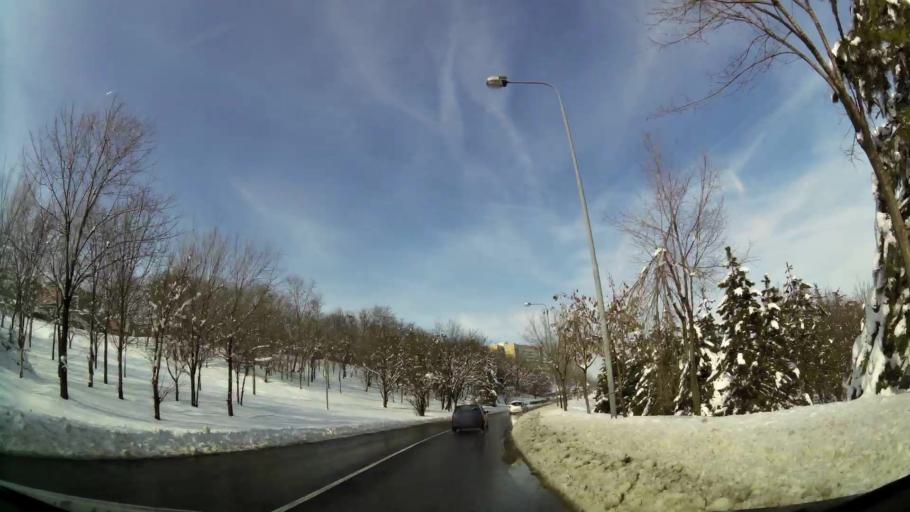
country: RS
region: Central Serbia
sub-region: Belgrade
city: Zvezdara
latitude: 44.7867
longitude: 20.5280
